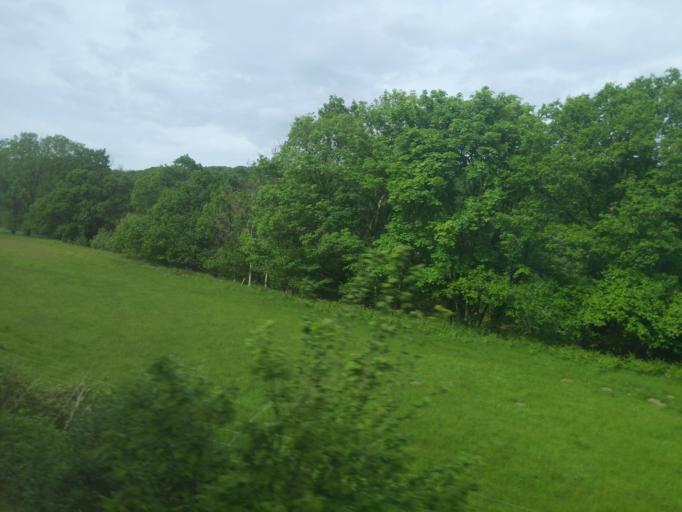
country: GB
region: England
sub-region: Devon
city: Winkleigh
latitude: 50.9567
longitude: -3.9289
